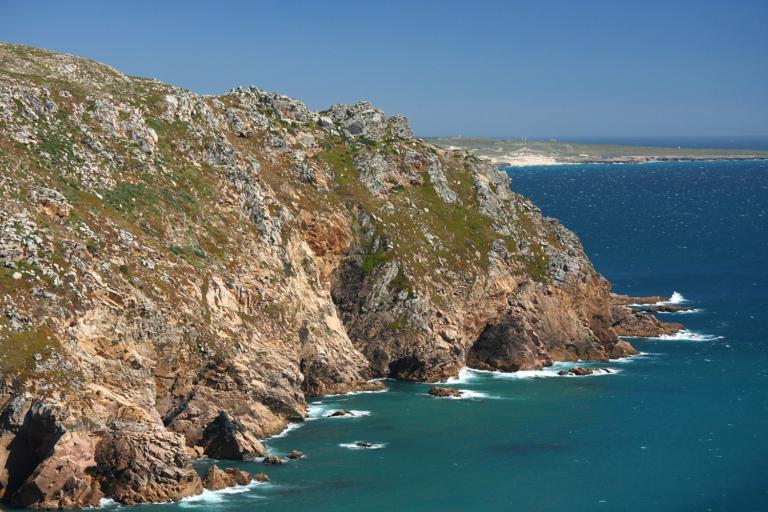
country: PT
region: Lisbon
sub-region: Sintra
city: Colares
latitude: 38.7789
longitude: -9.4982
